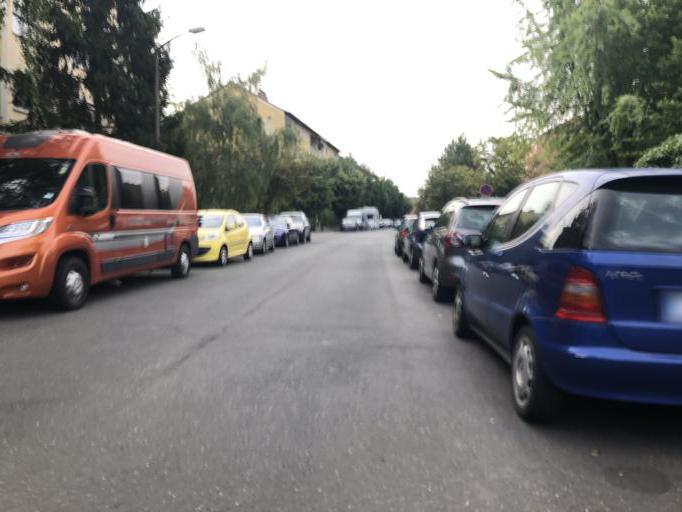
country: DE
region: Bavaria
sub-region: Regierungsbezirk Mittelfranken
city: Erlangen
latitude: 49.5781
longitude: 10.9957
